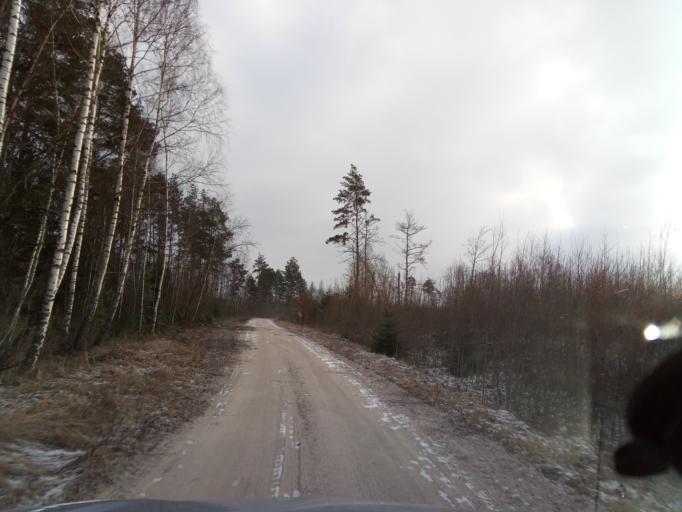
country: LT
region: Alytaus apskritis
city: Varena
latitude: 54.3680
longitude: 24.5470
